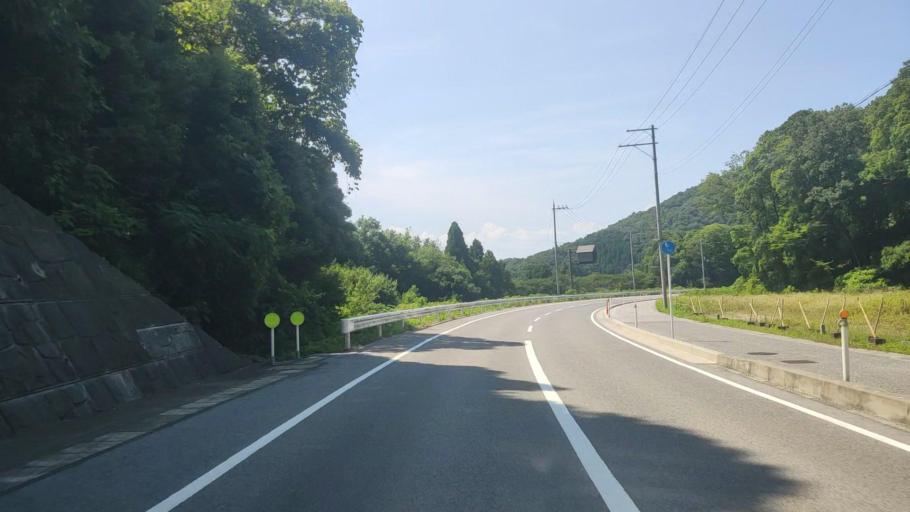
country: JP
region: Shiga Prefecture
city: Nagahama
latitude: 35.3840
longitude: 136.3329
